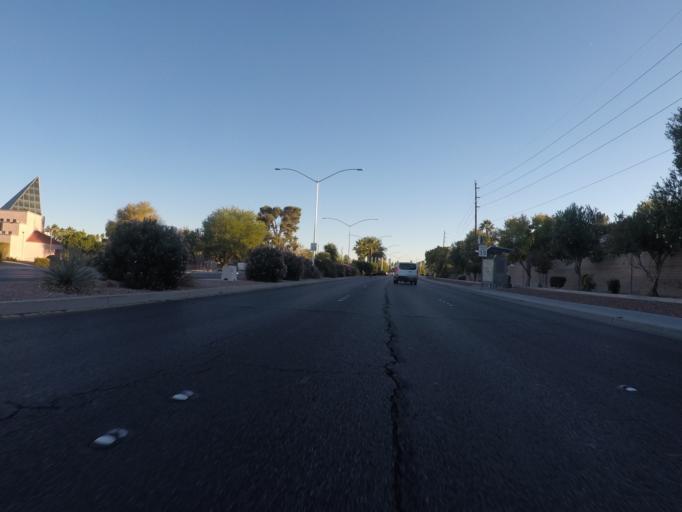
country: US
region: Nevada
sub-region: Clark County
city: Las Vegas
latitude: 36.1733
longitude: -115.1733
